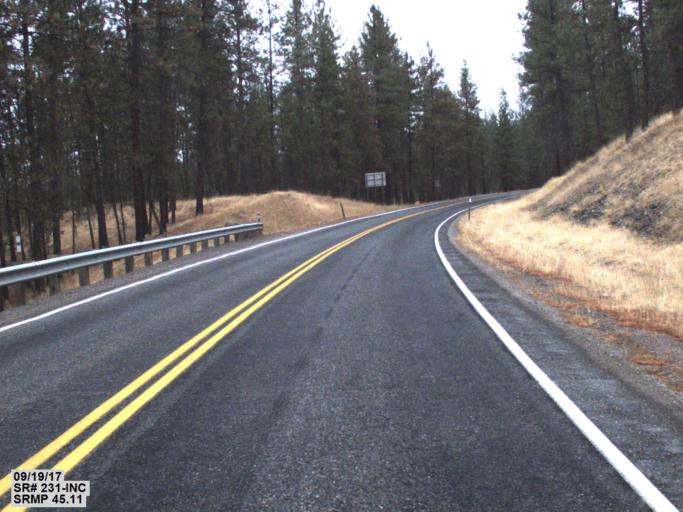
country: US
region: Washington
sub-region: Spokane County
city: Fairchild Air Force Base
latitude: 47.8440
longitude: -117.8559
